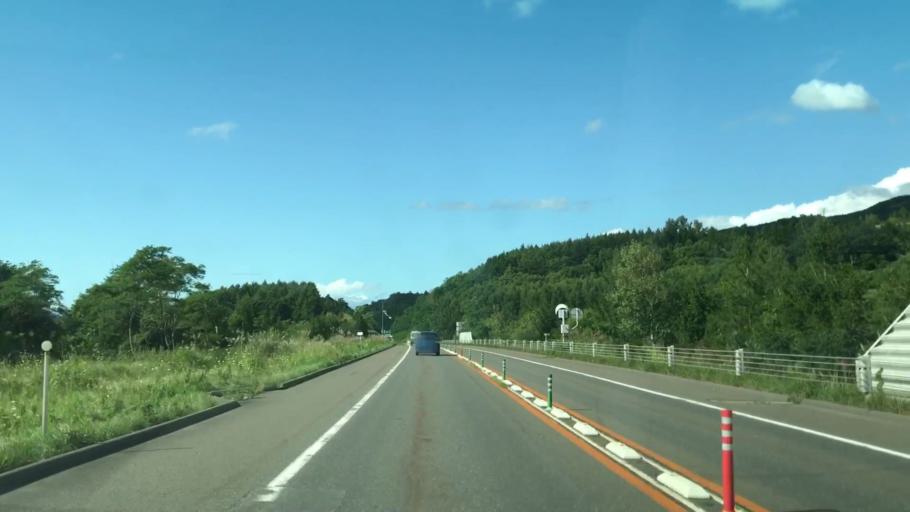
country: JP
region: Hokkaido
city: Date
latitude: 42.4525
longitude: 140.9132
